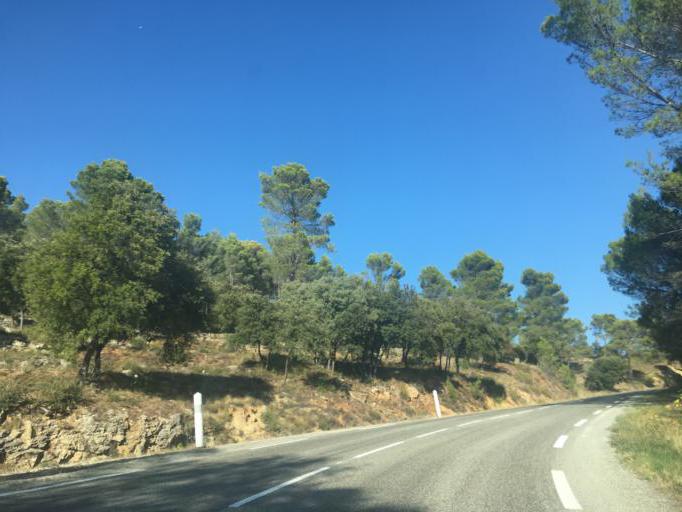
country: FR
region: Provence-Alpes-Cote d'Azur
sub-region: Departement du Var
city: Salernes
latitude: 43.5806
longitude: 6.2219
